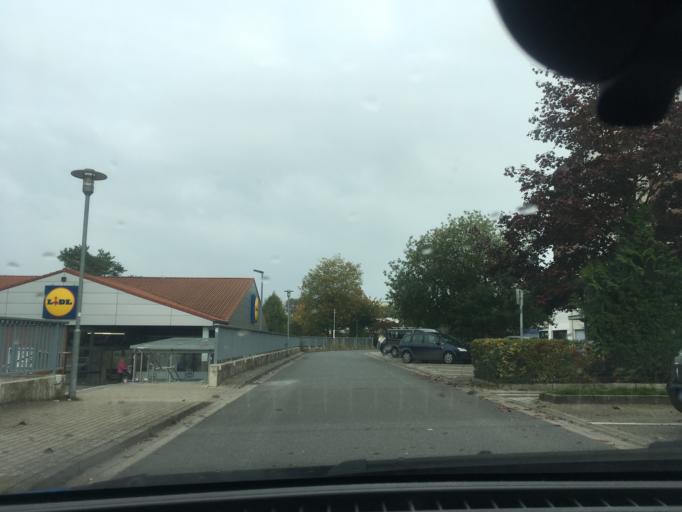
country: DE
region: Lower Saxony
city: Lueneburg
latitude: 53.2401
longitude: 10.4347
